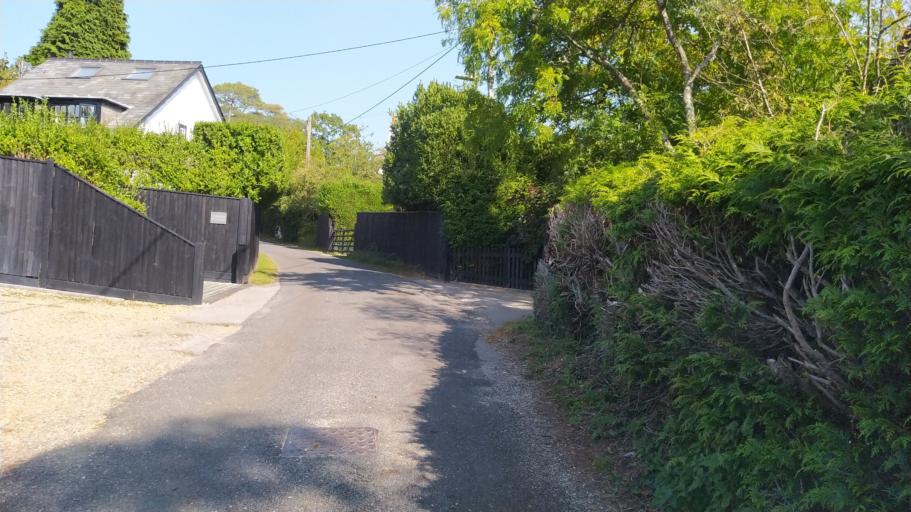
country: GB
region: England
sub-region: Hampshire
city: Lyndhurst
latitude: 50.8626
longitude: -1.5948
